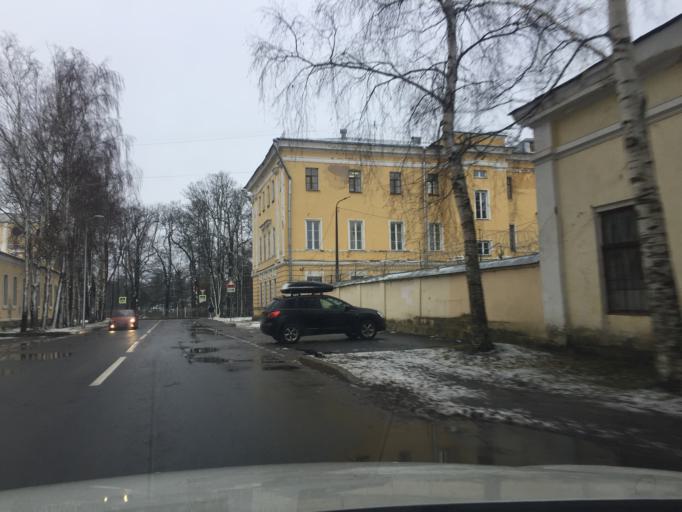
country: RU
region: St.-Petersburg
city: Pushkin
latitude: 59.7078
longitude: 30.3945
